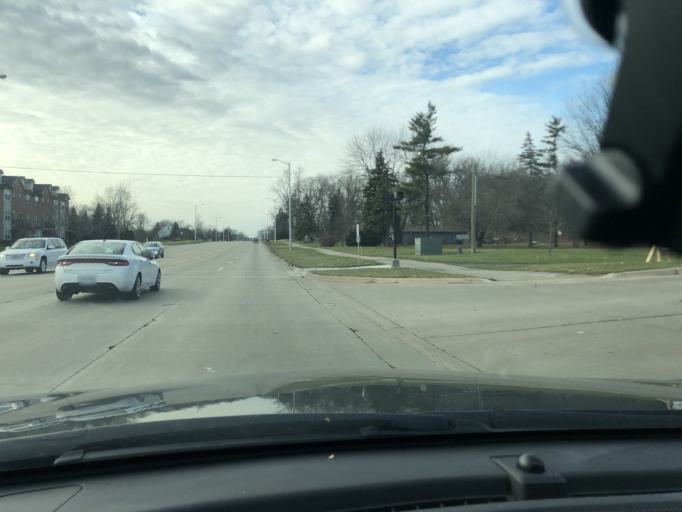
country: US
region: Michigan
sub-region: Wayne County
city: Taylor
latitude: 42.2126
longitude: -83.2485
